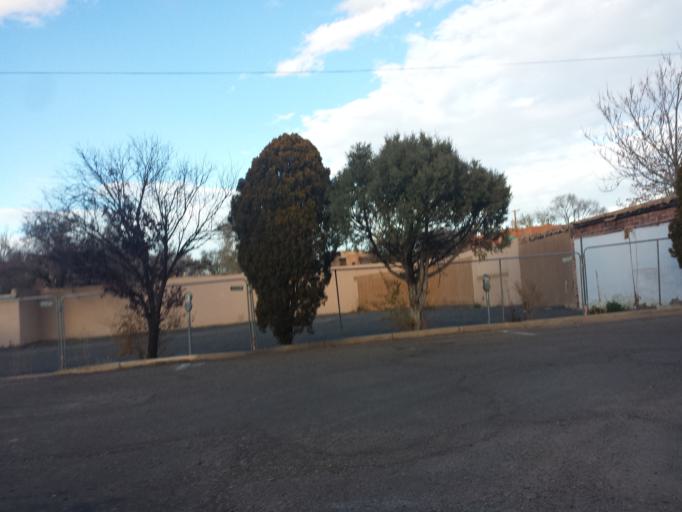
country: US
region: New Mexico
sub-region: Santa Fe County
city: Santa Fe
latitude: 35.6882
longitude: -105.9455
